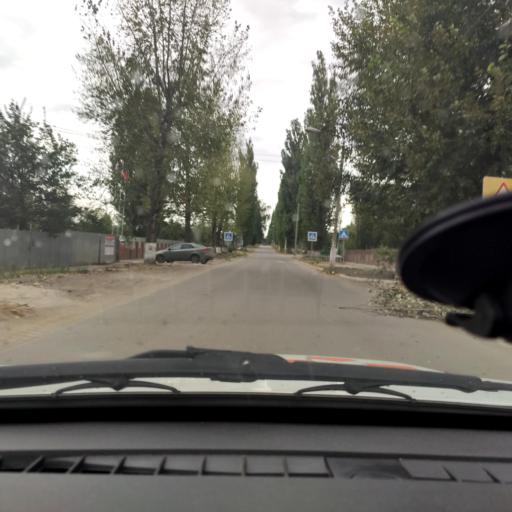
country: RU
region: Voronezj
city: Strelitsa
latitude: 51.6099
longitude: 38.9039
